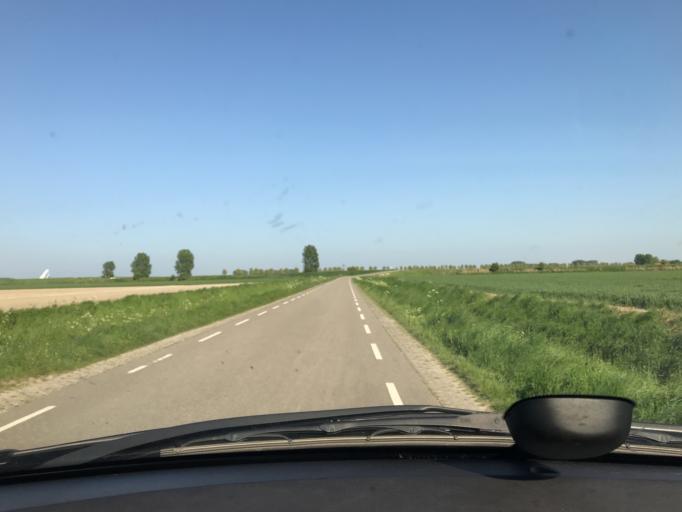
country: NL
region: Zeeland
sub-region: Gemeente Goes
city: Goes
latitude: 51.5383
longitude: 3.8383
